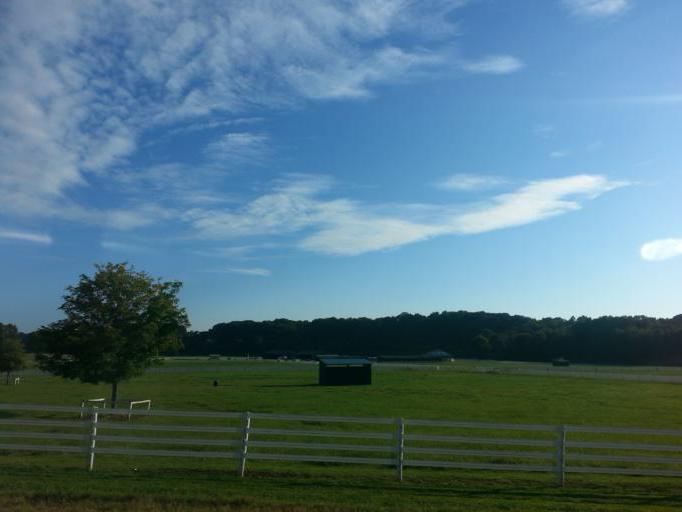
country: US
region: Alabama
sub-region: Lauderdale County
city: Rogersville
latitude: 34.8561
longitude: -87.4133
